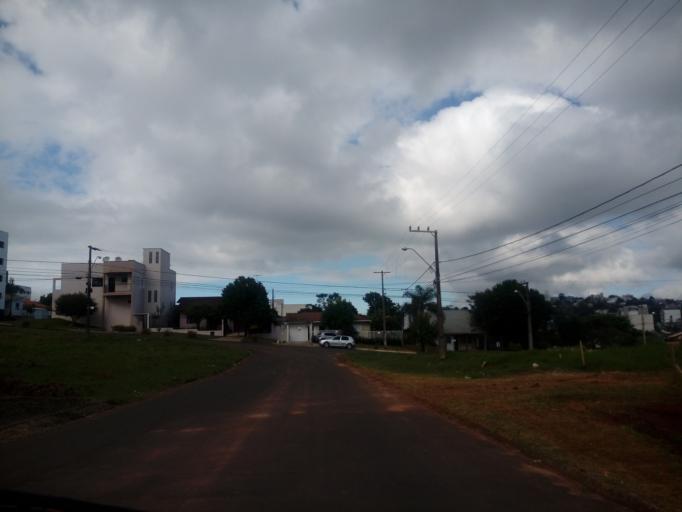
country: BR
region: Santa Catarina
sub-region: Chapeco
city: Chapeco
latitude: -27.1128
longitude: -52.6200
